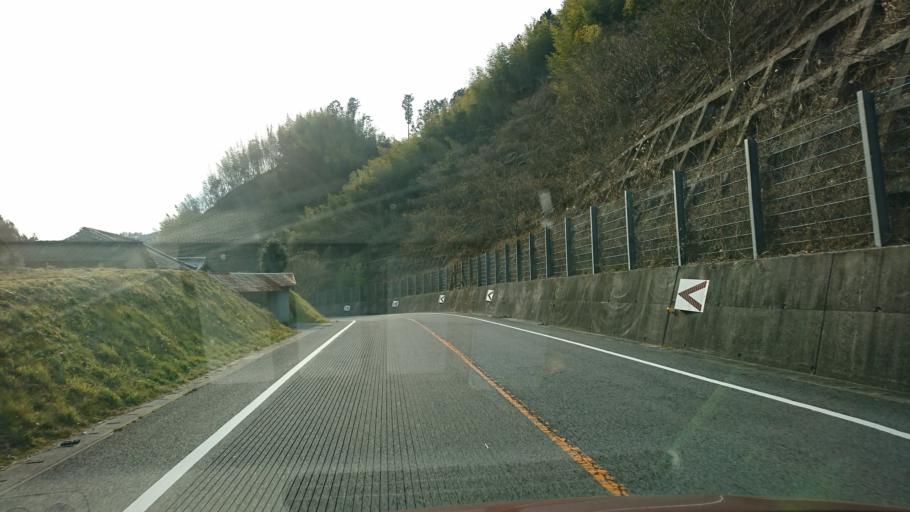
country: JP
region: Ehime
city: Hojo
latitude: 33.9254
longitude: 132.8908
